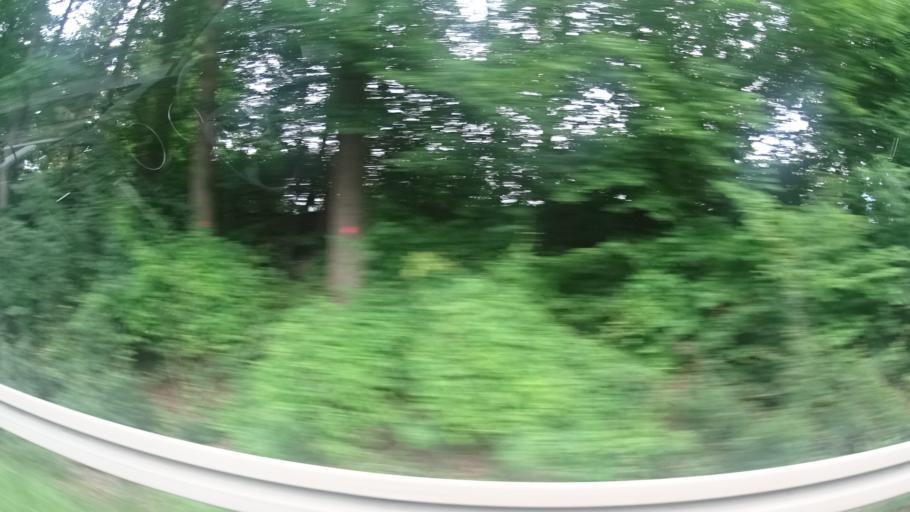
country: DE
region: Lower Saxony
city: Springe
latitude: 52.2133
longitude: 9.5915
